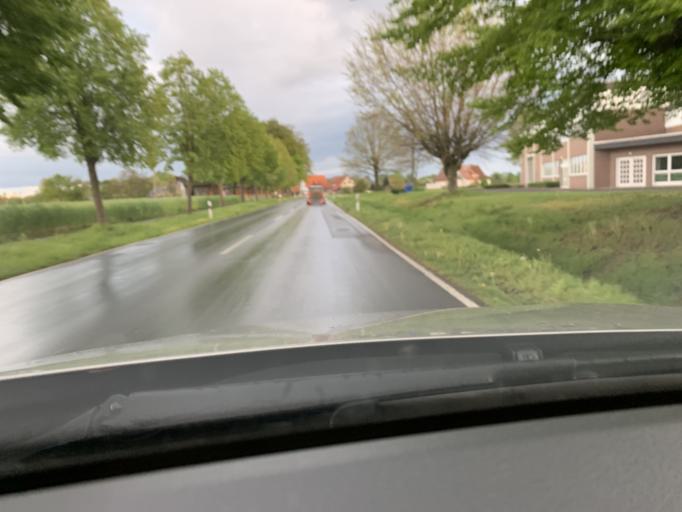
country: DE
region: North Rhine-Westphalia
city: Rietberg
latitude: 51.7613
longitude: 8.3865
